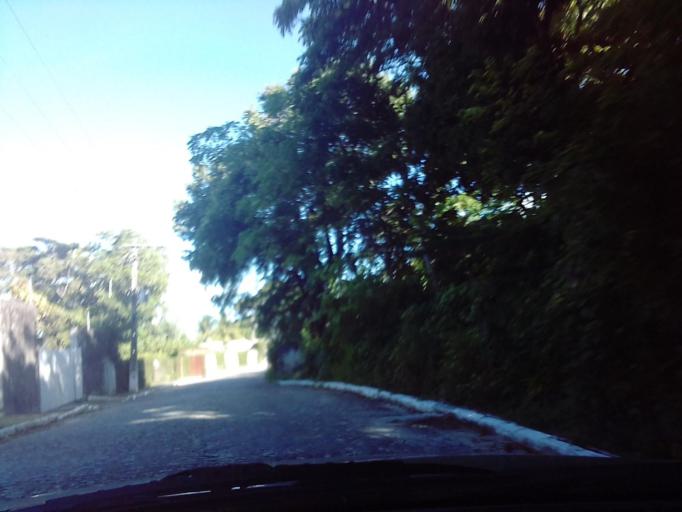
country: BR
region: Pernambuco
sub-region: Igarassu
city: Igarassu
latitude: -7.8465
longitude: -34.8430
